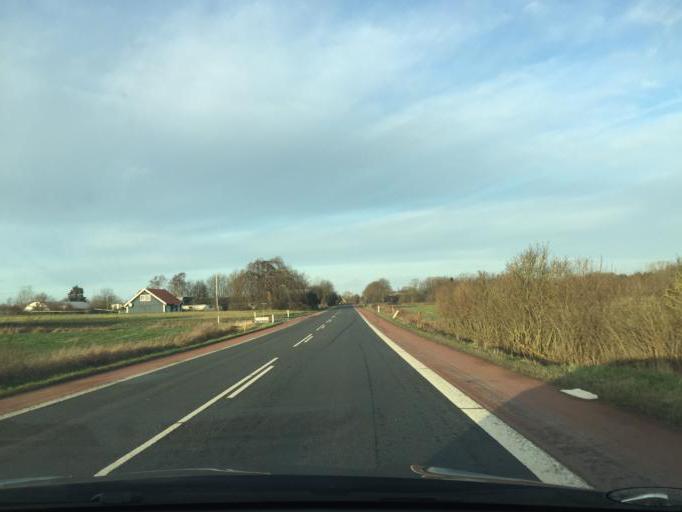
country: DK
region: South Denmark
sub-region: Faaborg-Midtfyn Kommune
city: Arslev
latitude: 55.2905
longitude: 10.4502
